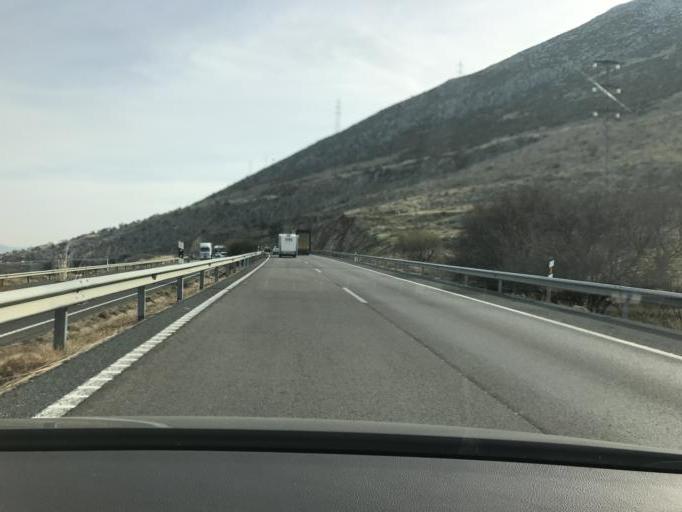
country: ES
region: Andalusia
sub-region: Provincia de Granada
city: Loja
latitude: 37.1600
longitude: -4.1496
